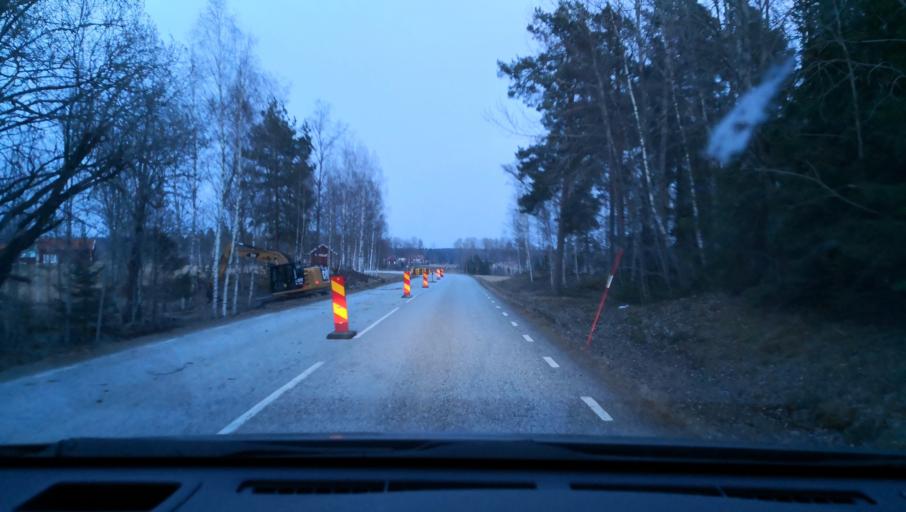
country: SE
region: OErebro
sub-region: Lindesbergs Kommun
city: Lindesberg
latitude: 59.5936
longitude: 15.2843
